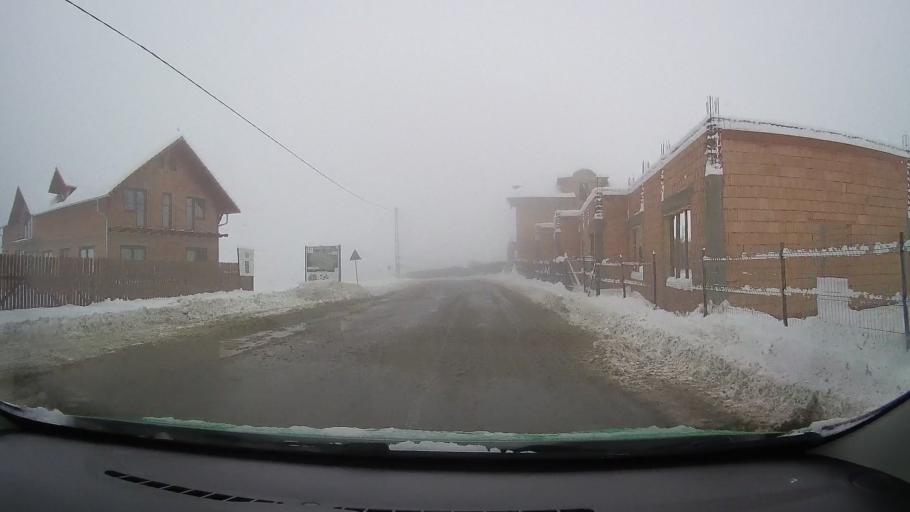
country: RO
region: Sibiu
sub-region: Comuna Jina
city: Jina
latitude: 45.7741
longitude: 23.6651
